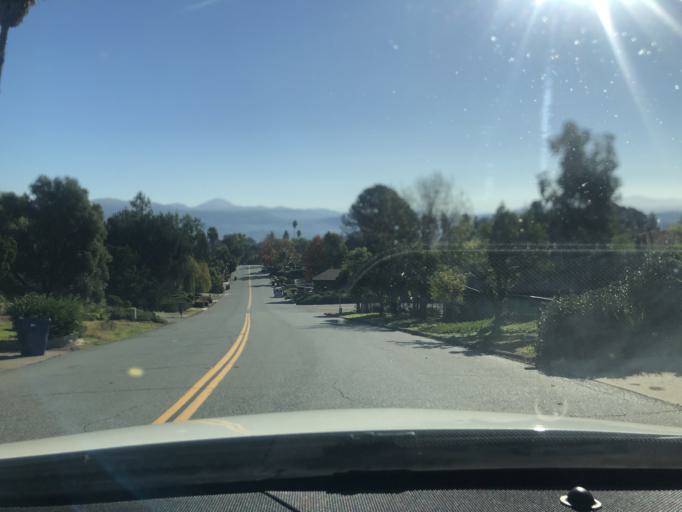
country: US
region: California
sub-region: San Diego County
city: Casa de Oro-Mount Helix
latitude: 32.7710
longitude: -116.9495
